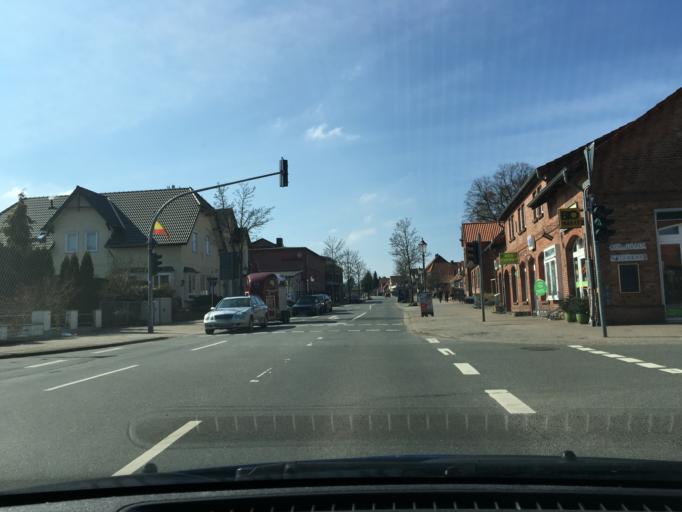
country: DE
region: Lower Saxony
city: Salzhausen
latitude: 53.2262
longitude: 10.1669
